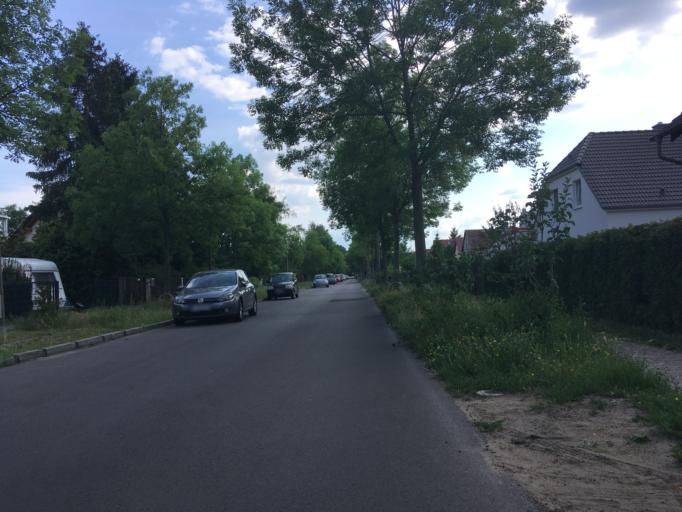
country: DE
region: Berlin
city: Adlershof
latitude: 52.4463
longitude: 13.5535
